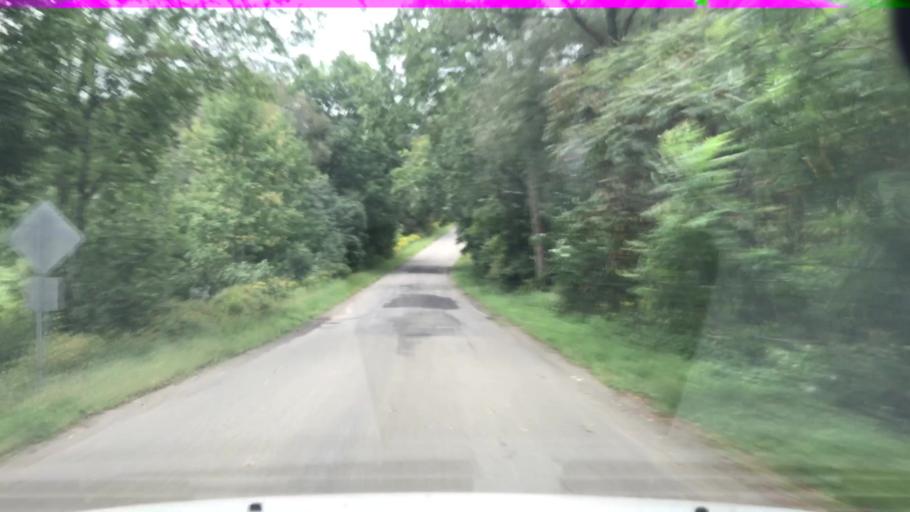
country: US
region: New York
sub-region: Cattaraugus County
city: Little Valley
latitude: 42.3210
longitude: -78.7239
